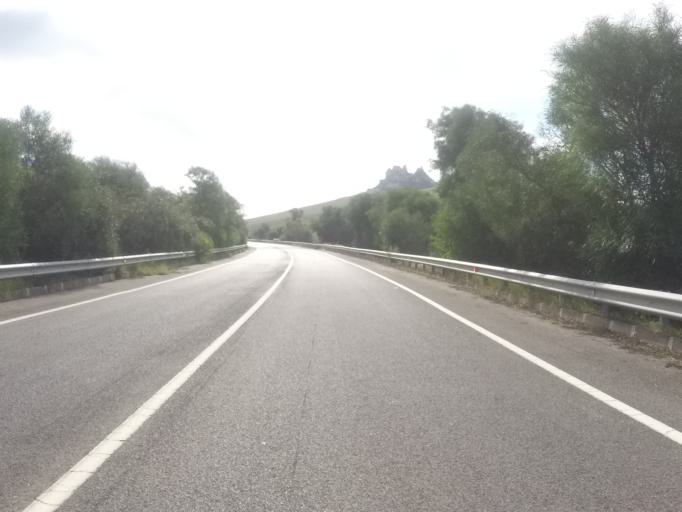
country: IT
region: Sicily
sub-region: Enna
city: Pietraperzia
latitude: 37.4477
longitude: 14.1168
